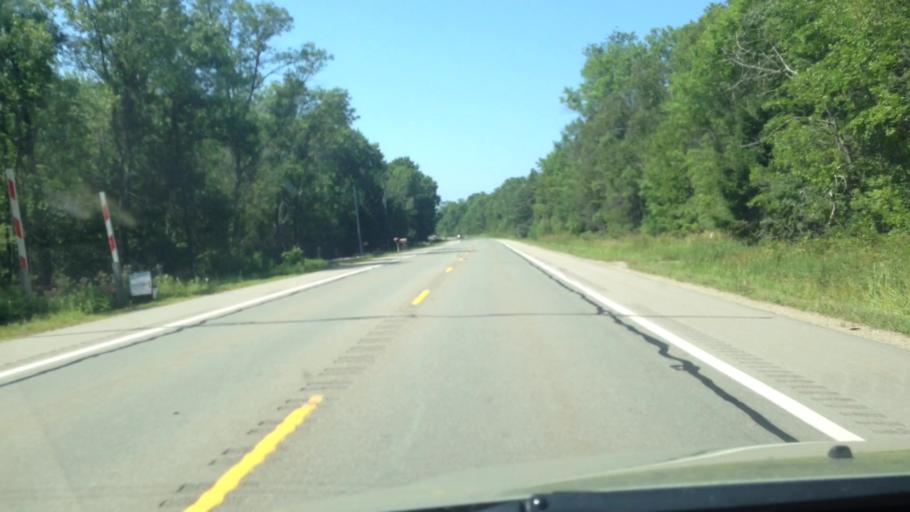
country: US
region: Michigan
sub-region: Menominee County
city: Menominee
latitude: 45.2409
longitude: -87.4979
